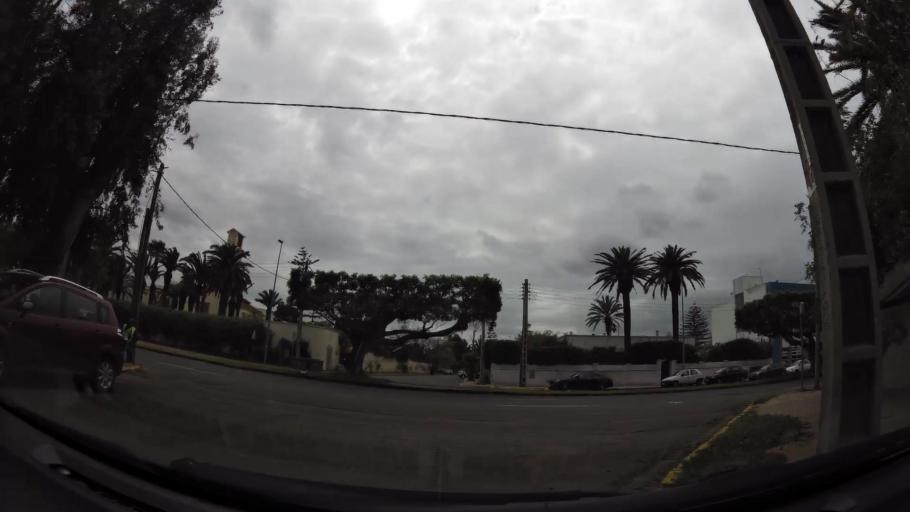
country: MA
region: Grand Casablanca
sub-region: Casablanca
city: Casablanca
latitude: 33.5586
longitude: -7.6369
